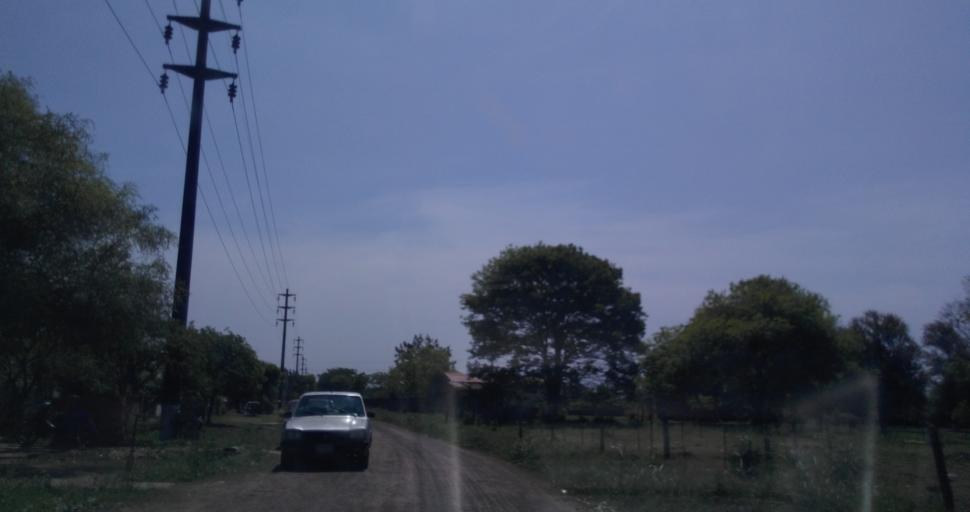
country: AR
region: Chaco
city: Fontana
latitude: -27.4025
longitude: -59.0002
